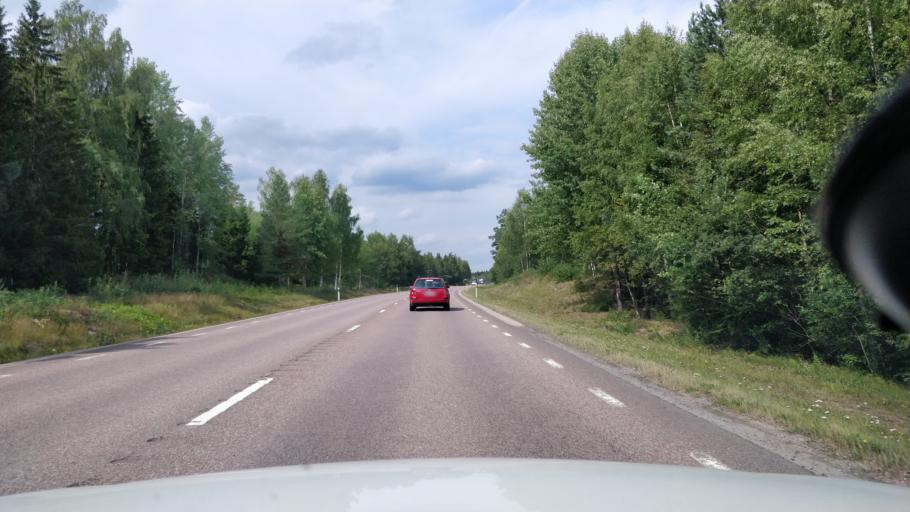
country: SE
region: Dalarna
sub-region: Faluns Kommun
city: Falun
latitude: 60.6422
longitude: 15.5761
